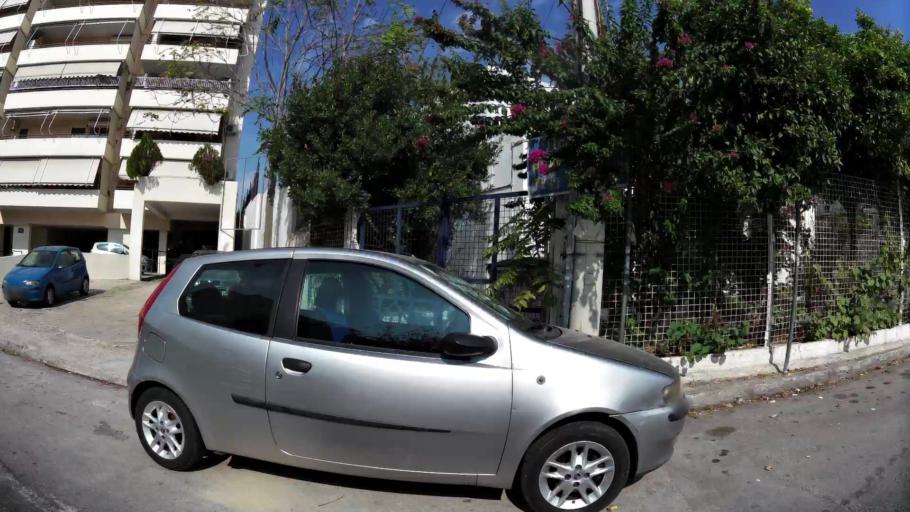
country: GR
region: Attica
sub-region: Nomarchia Athinas
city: Kipseli
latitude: 38.0096
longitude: 23.7207
